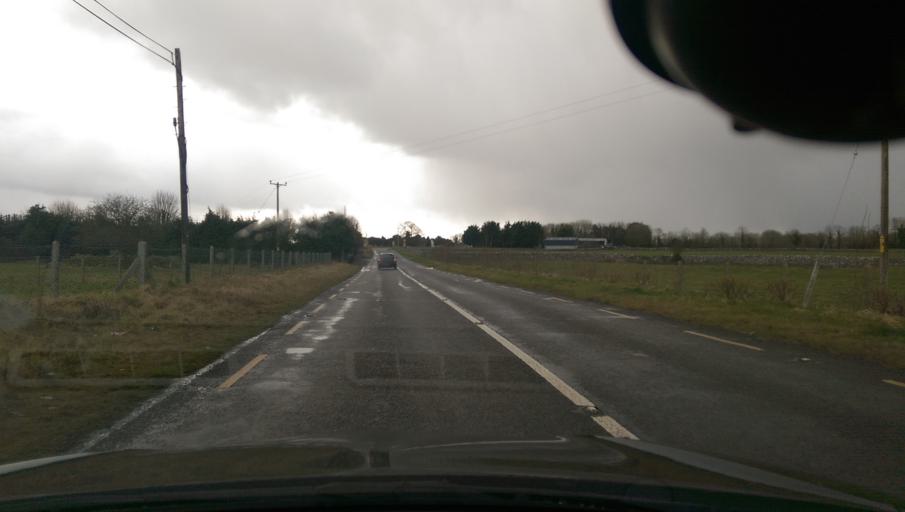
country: IE
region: Connaught
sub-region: County Galway
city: Athenry
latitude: 53.3507
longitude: -8.7497
